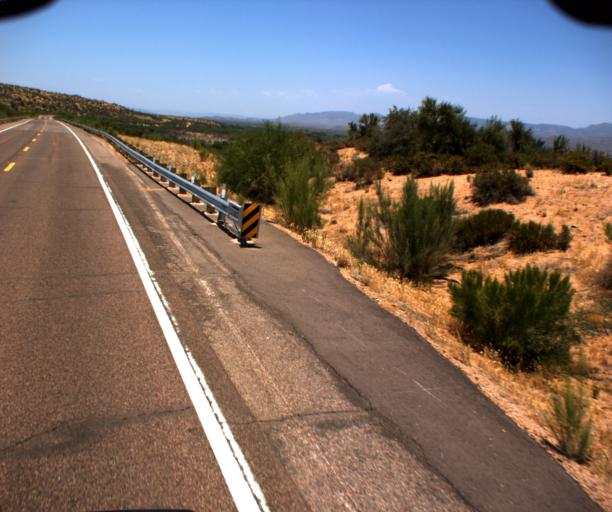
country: US
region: Arizona
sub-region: Gila County
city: Tonto Basin
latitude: 33.7734
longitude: -111.2606
